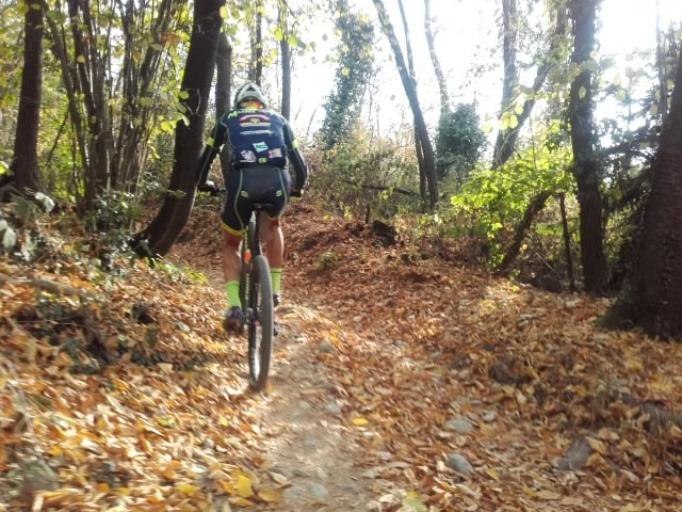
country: IT
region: Piedmont
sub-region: Provincia di Torino
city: San Mauro Torinese
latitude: 45.0745
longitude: 7.7669
